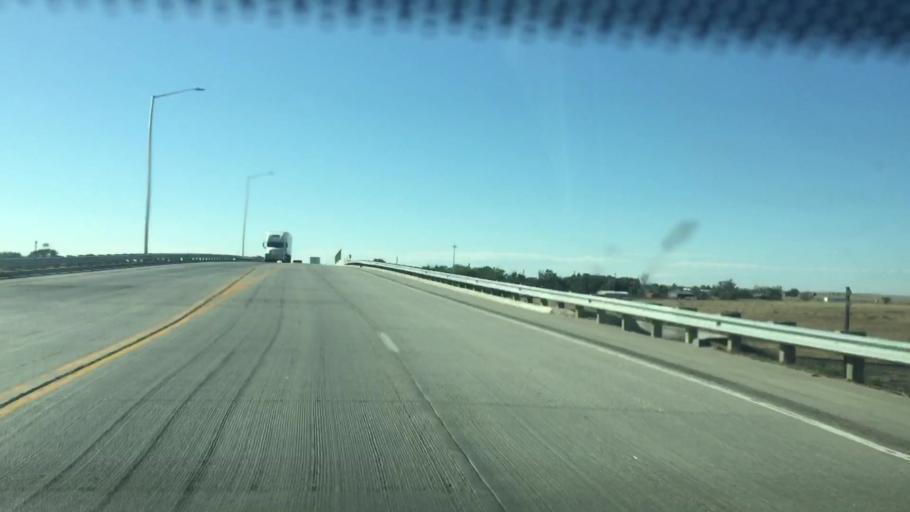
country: US
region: Colorado
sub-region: Kiowa County
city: Eads
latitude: 38.7630
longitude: -102.7813
